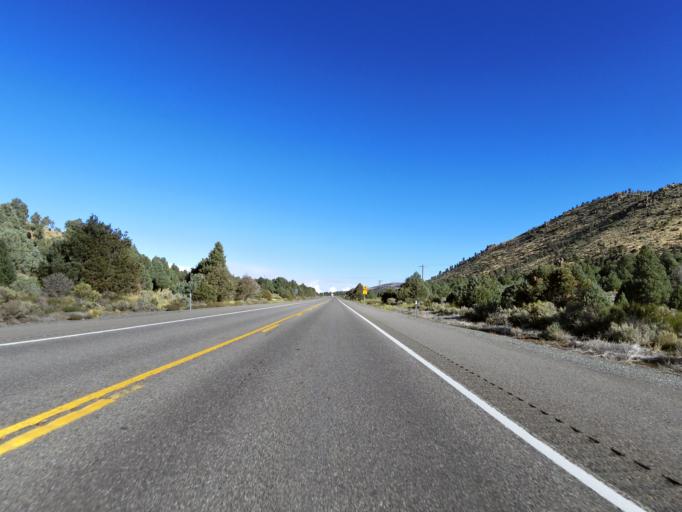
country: US
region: Nevada
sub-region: Douglas County
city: Gardnerville Ranchos
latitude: 38.7707
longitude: -119.5808
